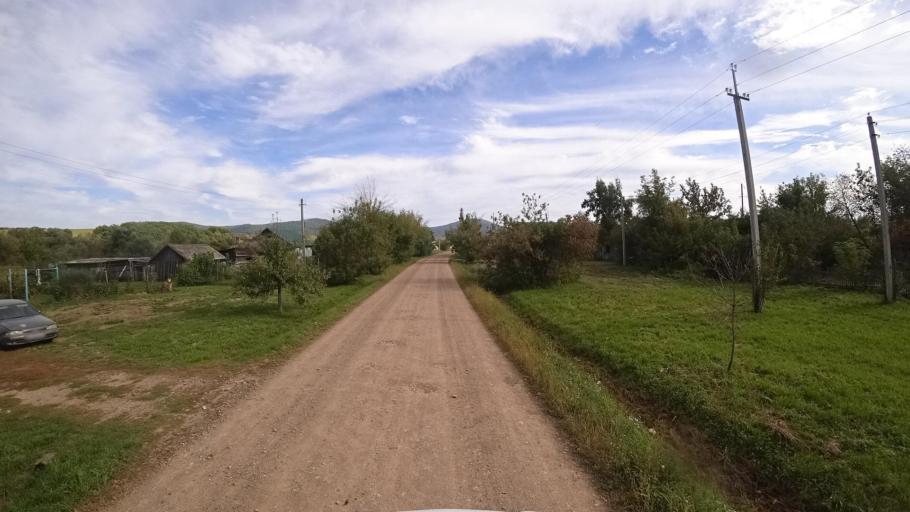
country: RU
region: Primorskiy
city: Dostoyevka
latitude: 44.3034
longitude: 133.4620
